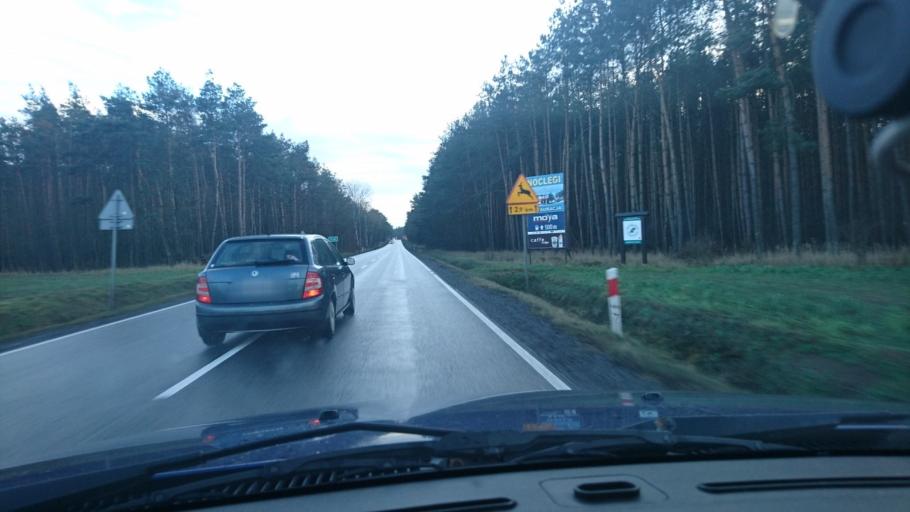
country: PL
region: Greater Poland Voivodeship
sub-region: Powiat kepinski
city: Bralin
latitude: 51.3465
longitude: 17.9506
